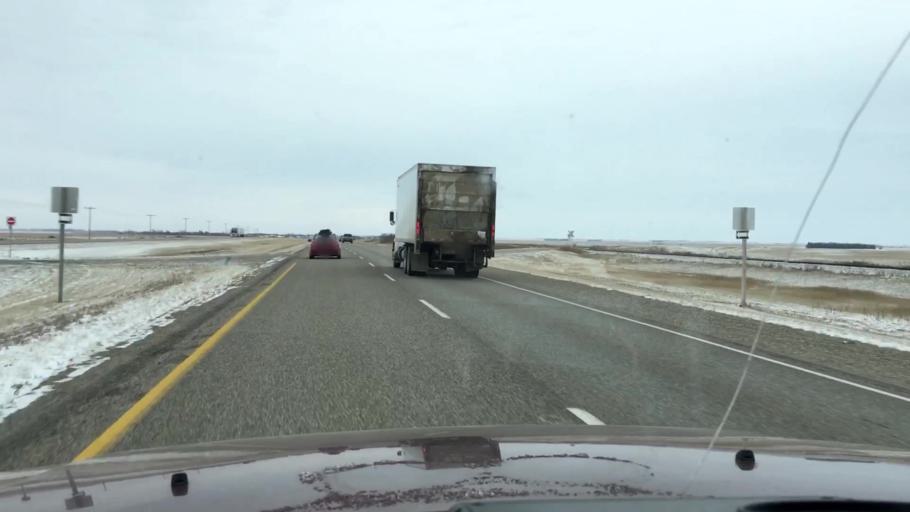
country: CA
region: Saskatchewan
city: Watrous
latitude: 51.1799
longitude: -105.9388
